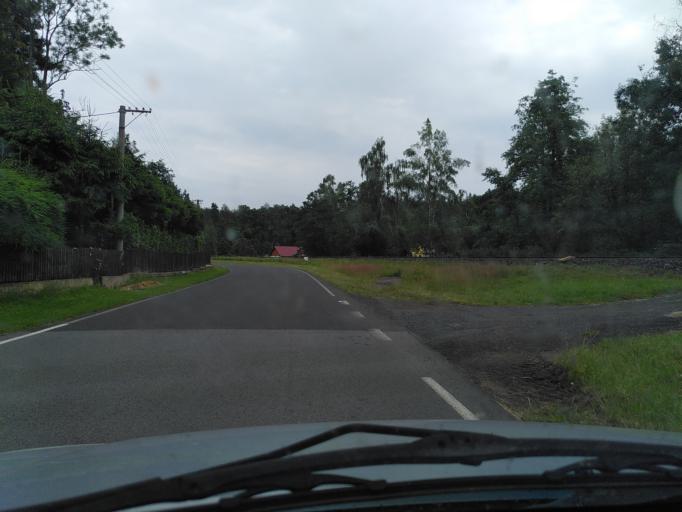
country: CZ
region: Ustecky
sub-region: Okres Decin
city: Chribska
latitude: 50.8139
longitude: 14.5114
